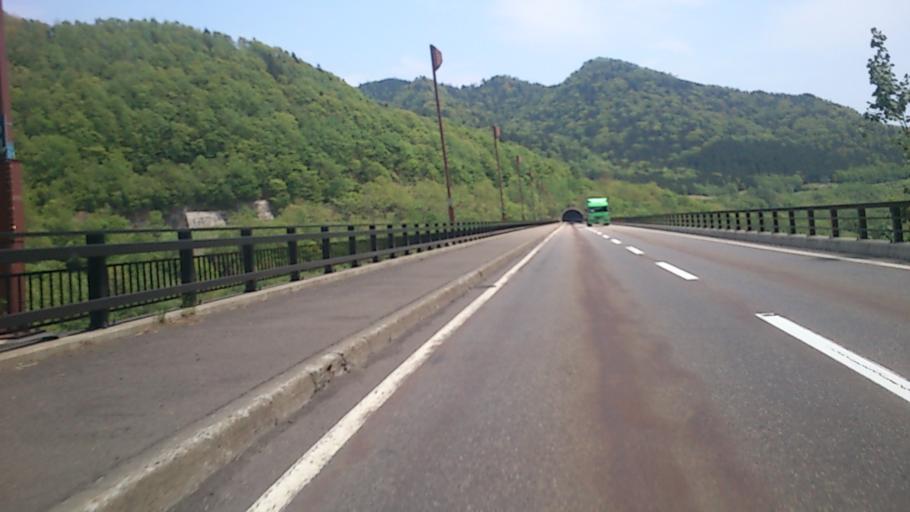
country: JP
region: Hokkaido
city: Otofuke
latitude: 43.3712
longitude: 143.2162
